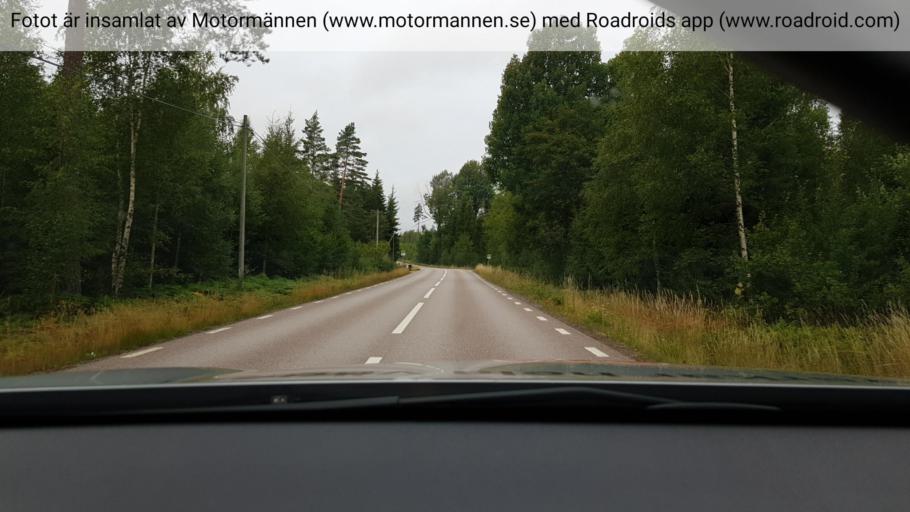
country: SE
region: Soedermanland
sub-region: Strangnas Kommun
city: Mariefred
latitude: 59.1539
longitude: 17.1765
